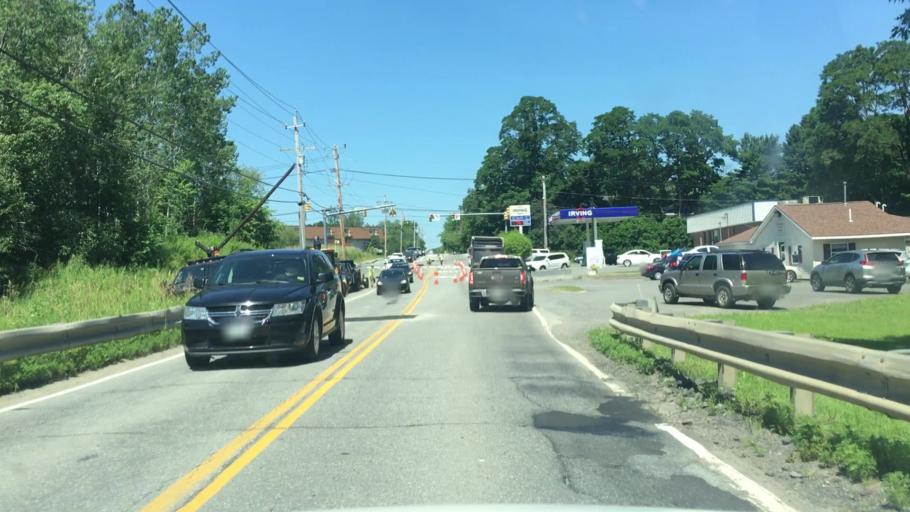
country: US
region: Maine
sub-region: Penobscot County
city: Bangor
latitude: 44.8238
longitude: -68.8081
